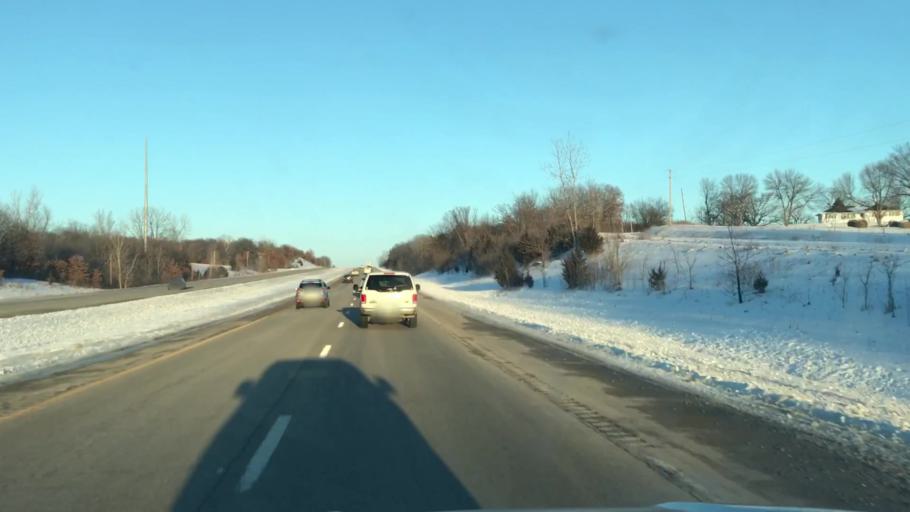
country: US
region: Missouri
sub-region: Clinton County
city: Gower
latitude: 39.7508
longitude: -94.5958
